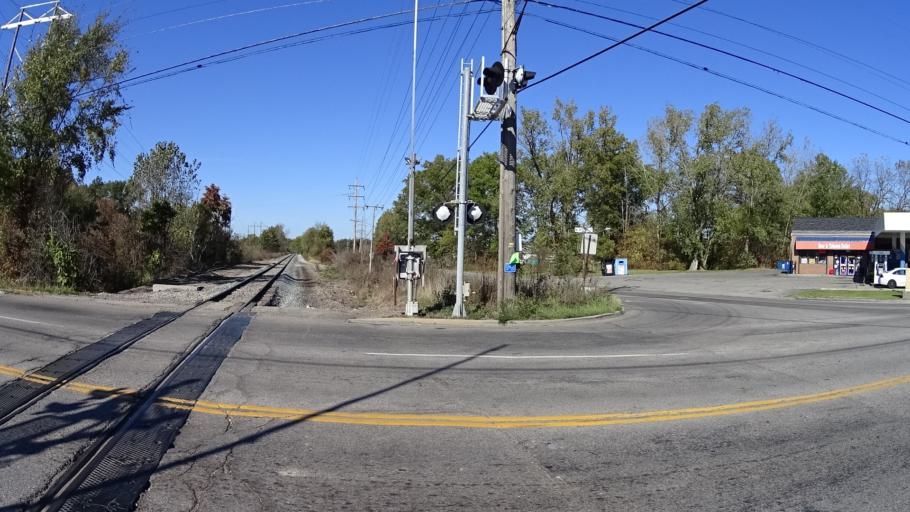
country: US
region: Ohio
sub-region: Lorain County
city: Sheffield
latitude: 41.4181
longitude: -82.1346
